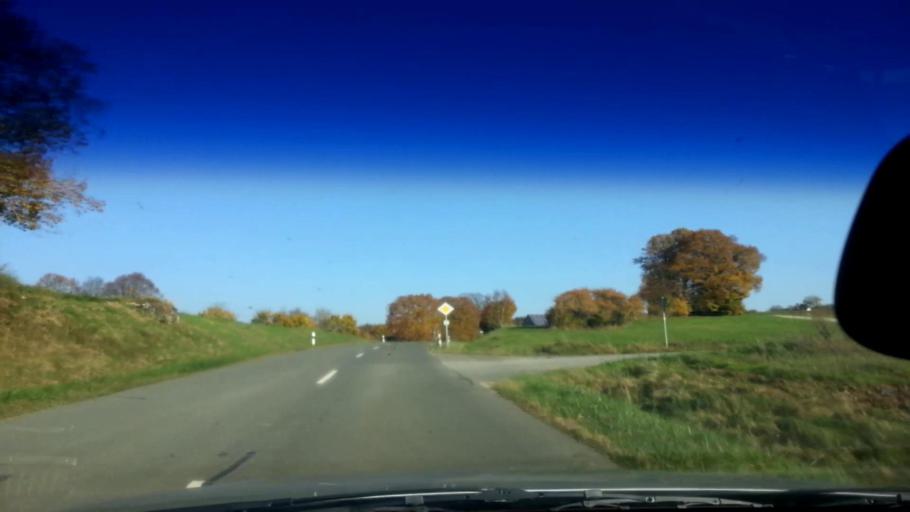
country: DE
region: Bavaria
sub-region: Upper Franconia
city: Wonsees
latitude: 49.9806
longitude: 11.3074
